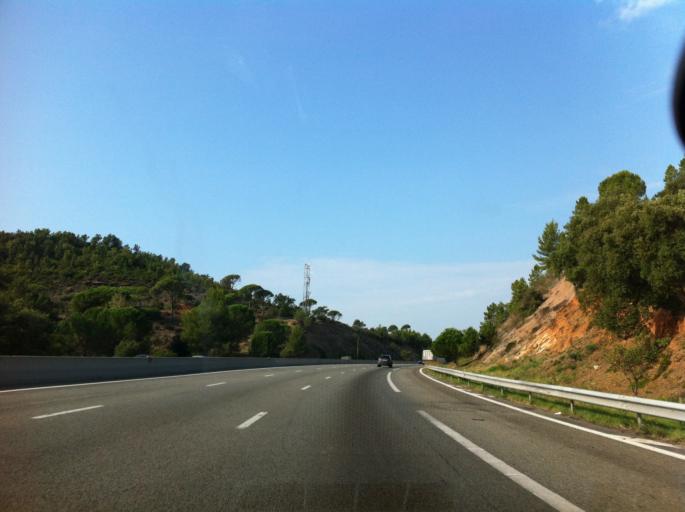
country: FR
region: Provence-Alpes-Cote d'Azur
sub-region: Departement du Var
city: Vidauban
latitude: 43.4174
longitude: 6.4630
